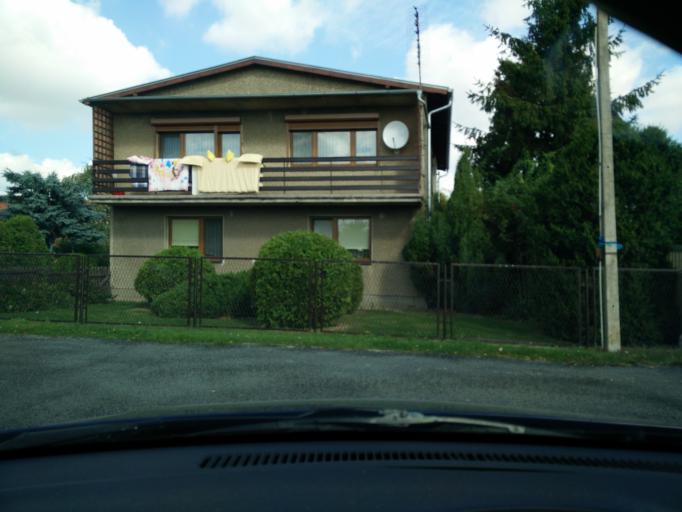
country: PL
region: Greater Poland Voivodeship
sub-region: Powiat sredzki
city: Dominowo
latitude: 52.2888
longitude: 17.3878
